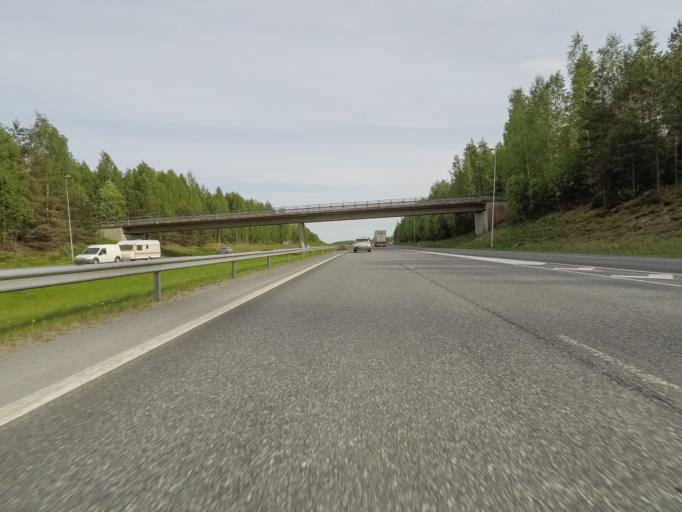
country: FI
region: Haeme
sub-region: Haemeenlinna
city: Janakkala
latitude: 60.9092
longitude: 24.5470
